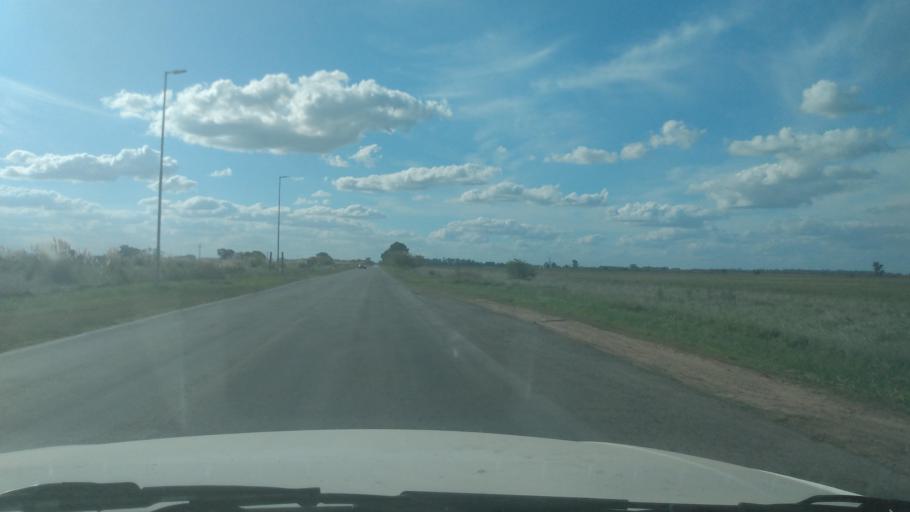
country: AR
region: Buenos Aires
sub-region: Partido de Navarro
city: Navarro
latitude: -34.9853
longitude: -59.3157
